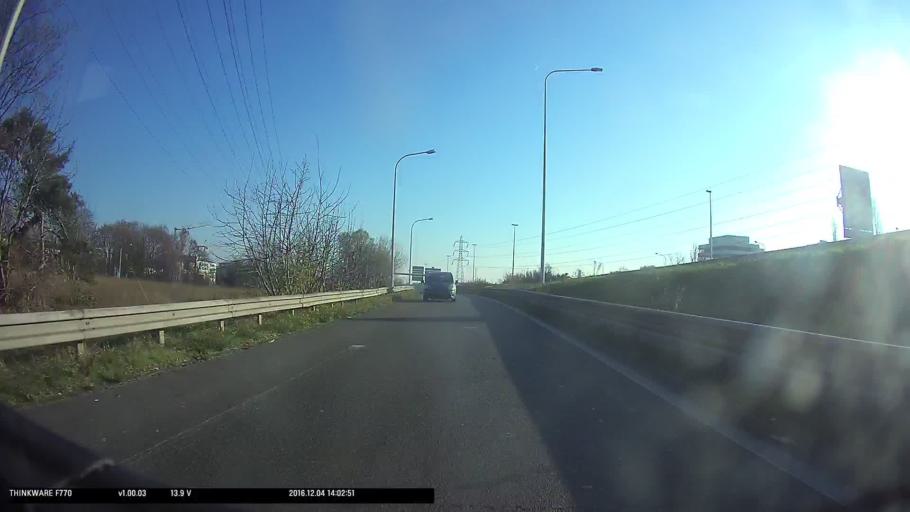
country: FR
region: Ile-de-France
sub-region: Departement du Val-d'Oise
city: Cergy-Pontoise
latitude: 49.0431
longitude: 2.0786
